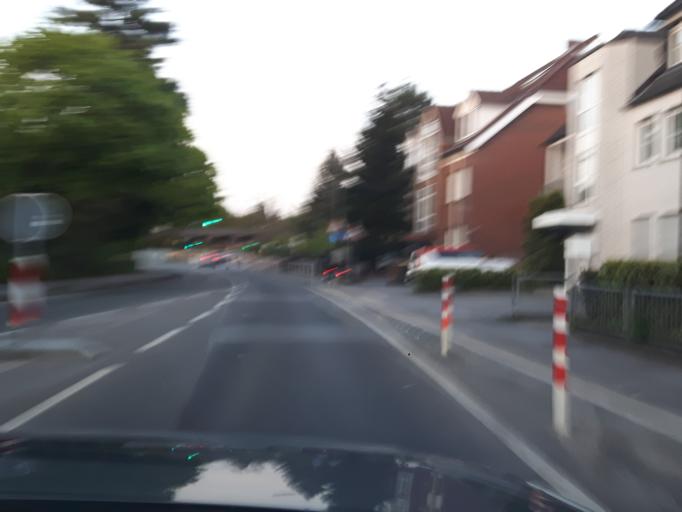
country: DE
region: North Rhine-Westphalia
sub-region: Regierungsbezirk Dusseldorf
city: Ratingen
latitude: 51.3296
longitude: 6.8294
